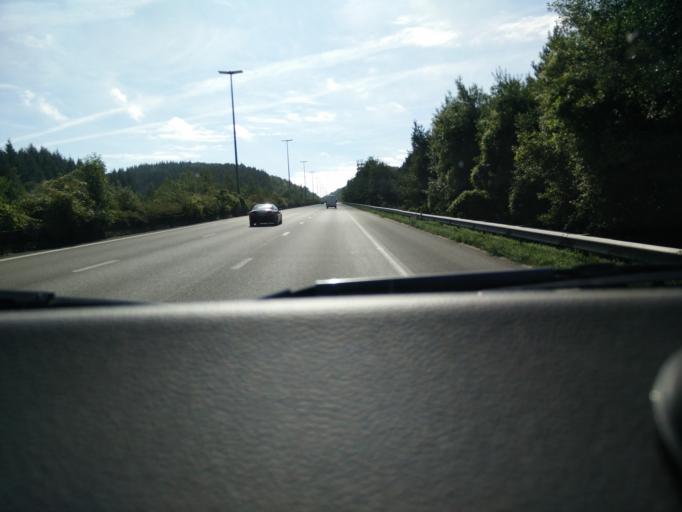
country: BE
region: Wallonia
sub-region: Province du Luxembourg
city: Tellin
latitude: 50.0774
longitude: 5.1749
